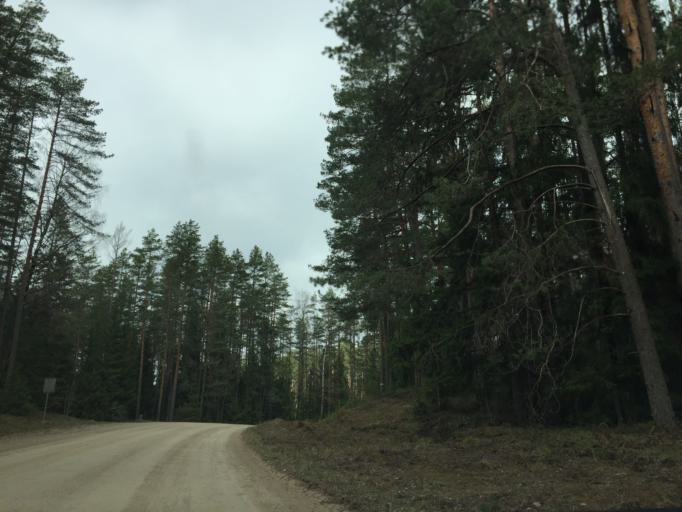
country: EE
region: Valgamaa
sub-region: Valga linn
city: Valga
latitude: 57.5829
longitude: 26.2227
